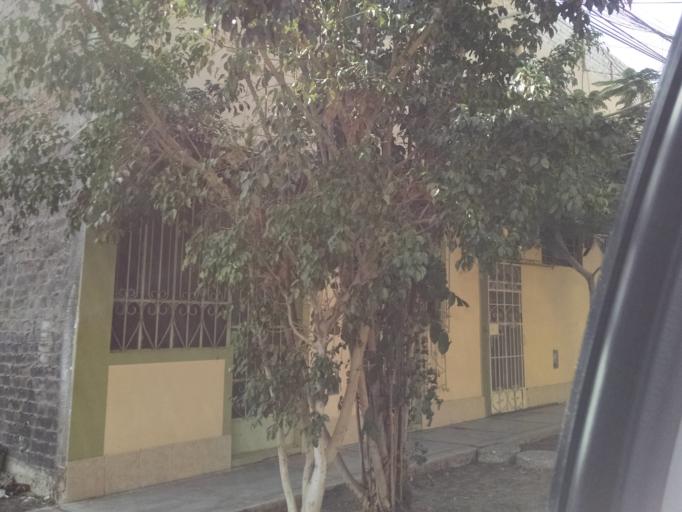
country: PE
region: Piura
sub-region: Provincia de Piura
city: Piura
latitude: -5.1702
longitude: -80.6332
